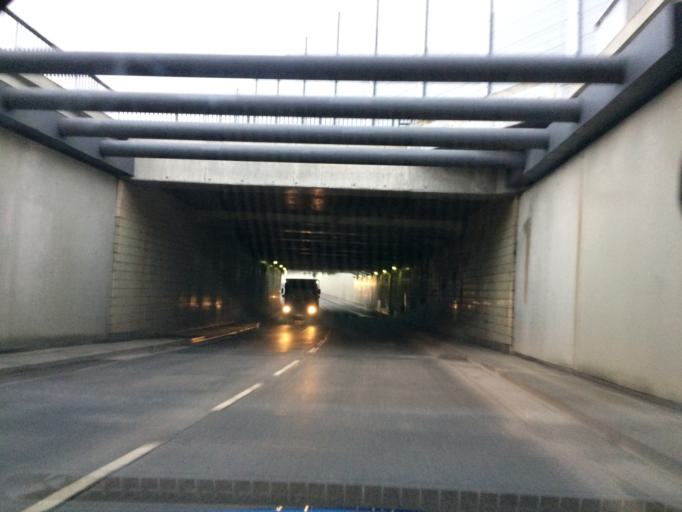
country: DE
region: Lower Saxony
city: Winsen
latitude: 53.3538
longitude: 10.2064
